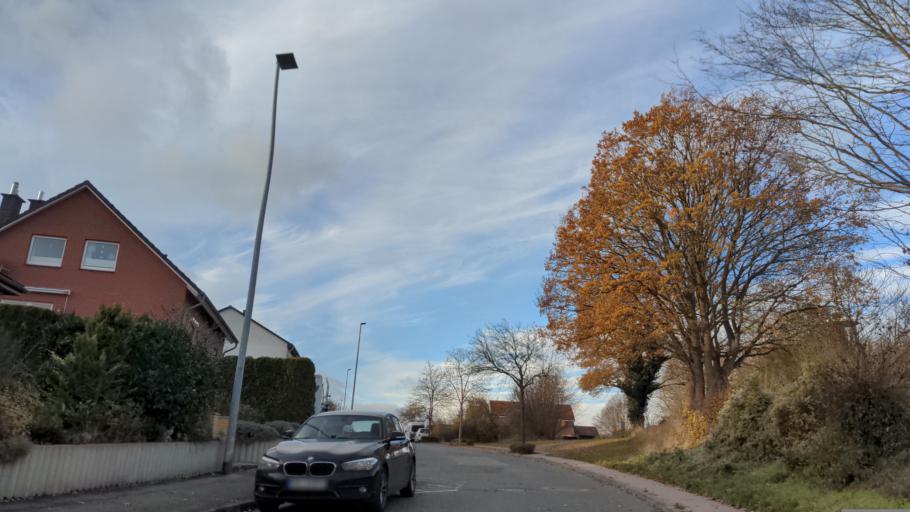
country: DE
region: Schleswig-Holstein
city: Neustadt in Holstein
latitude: 54.0972
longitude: 10.8291
